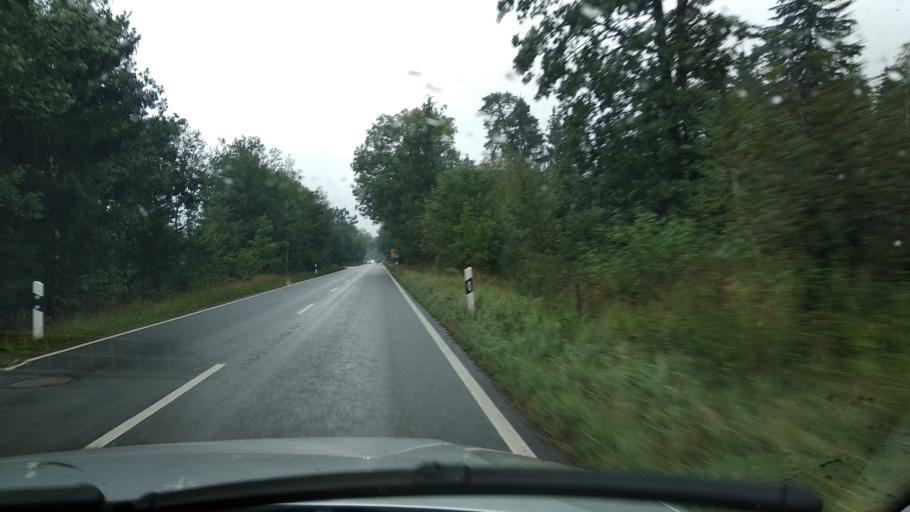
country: DE
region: Bavaria
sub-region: Upper Bavaria
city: Hohenbrunn
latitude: 48.0289
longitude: 11.7014
